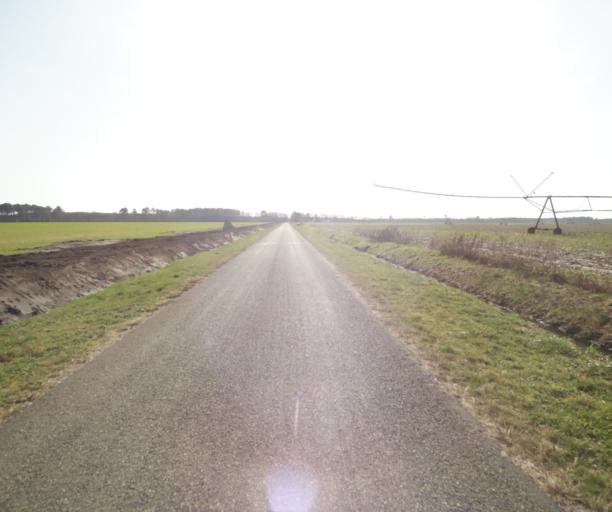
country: FR
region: Aquitaine
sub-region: Departement des Landes
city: Roquefort
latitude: 44.1532
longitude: -0.1710
